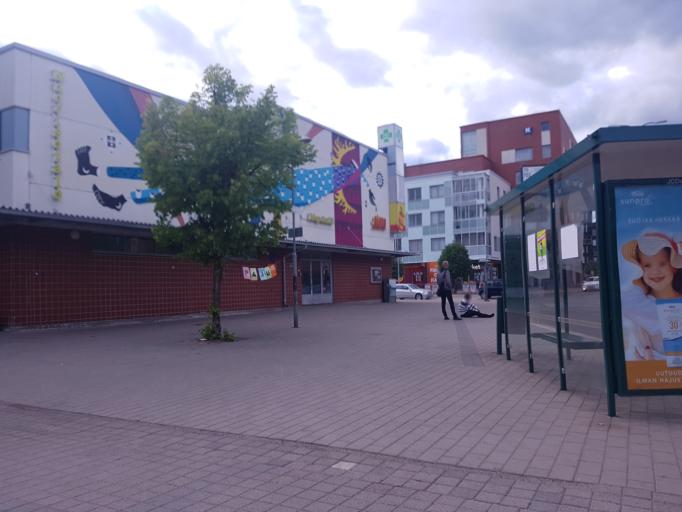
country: FI
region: Uusimaa
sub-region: Helsinki
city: Vantaa
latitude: 60.2431
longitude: 24.9946
